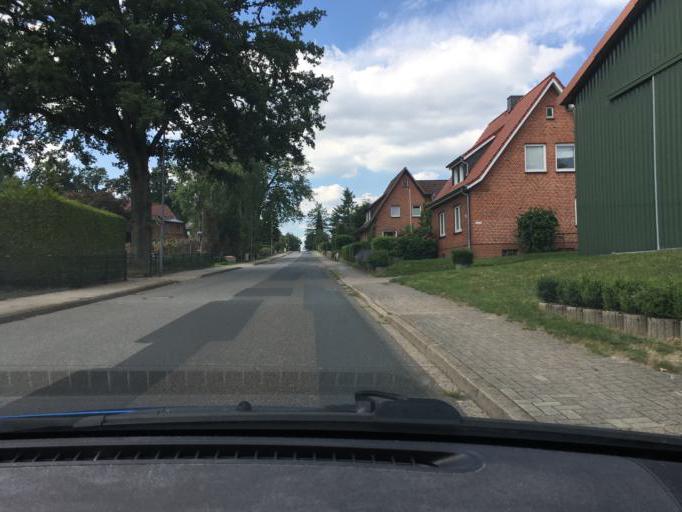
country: DE
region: Lower Saxony
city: Buchholz in der Nordheide
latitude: 53.3676
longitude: 9.8701
